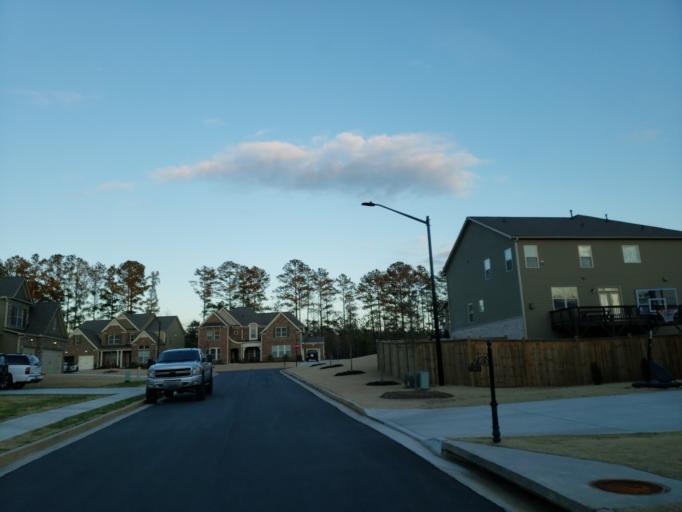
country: US
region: Georgia
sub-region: Cobb County
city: Acworth
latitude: 33.9741
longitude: -84.7084
